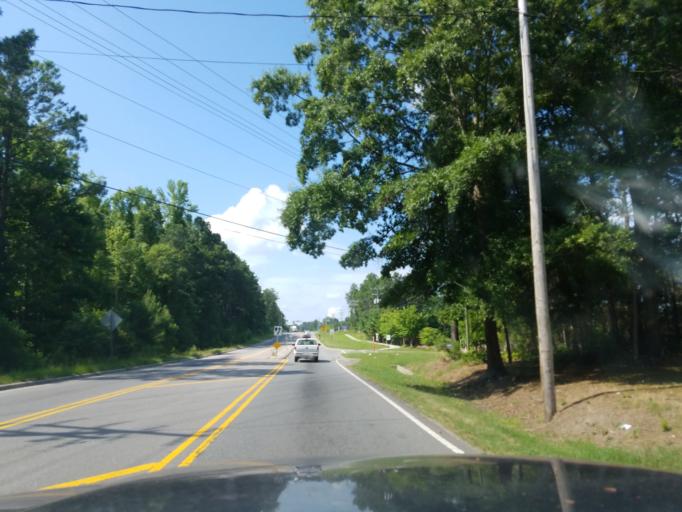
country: US
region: North Carolina
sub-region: Durham County
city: Durham
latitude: 35.9454
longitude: -78.9046
